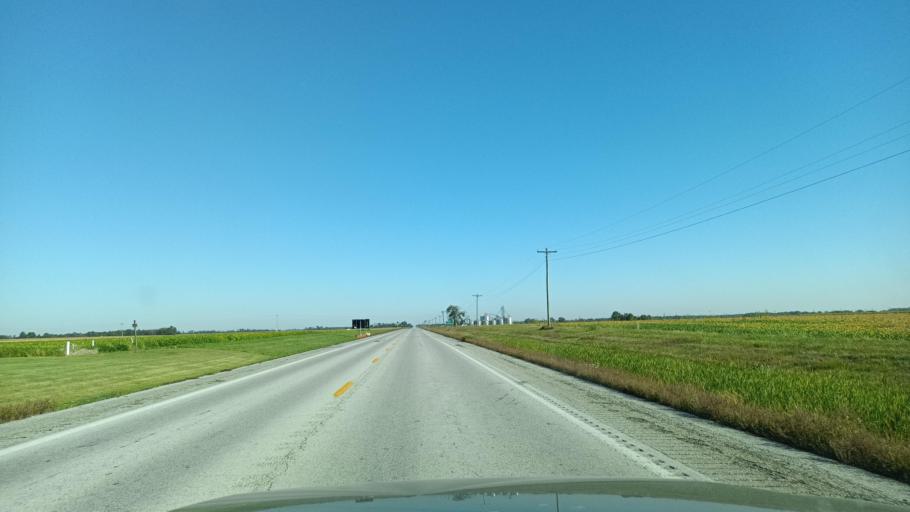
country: US
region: Missouri
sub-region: Audrain County
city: Vandalia
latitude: 39.3568
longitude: -91.6426
